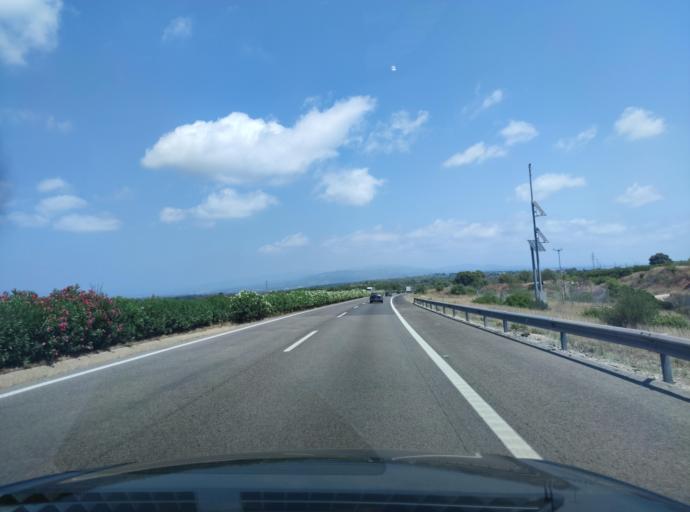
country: ES
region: Catalonia
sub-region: Provincia de Tarragona
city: Masdenverge
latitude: 40.6857
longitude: 0.5269
